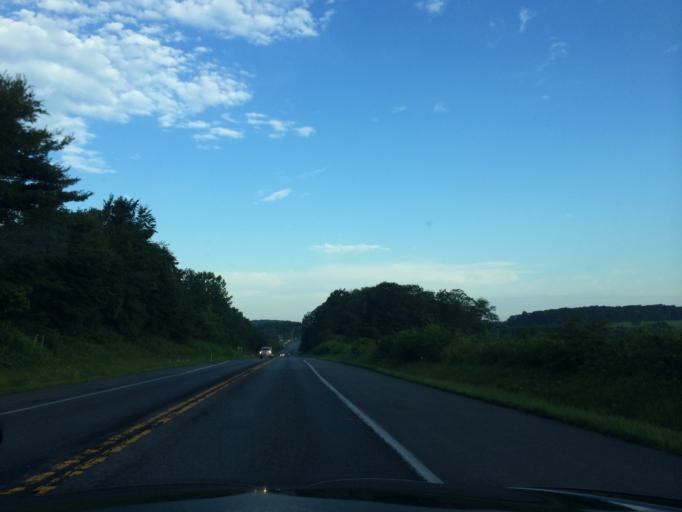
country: US
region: Maryland
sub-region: Carroll County
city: Eldersburg
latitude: 39.4362
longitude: -77.0208
